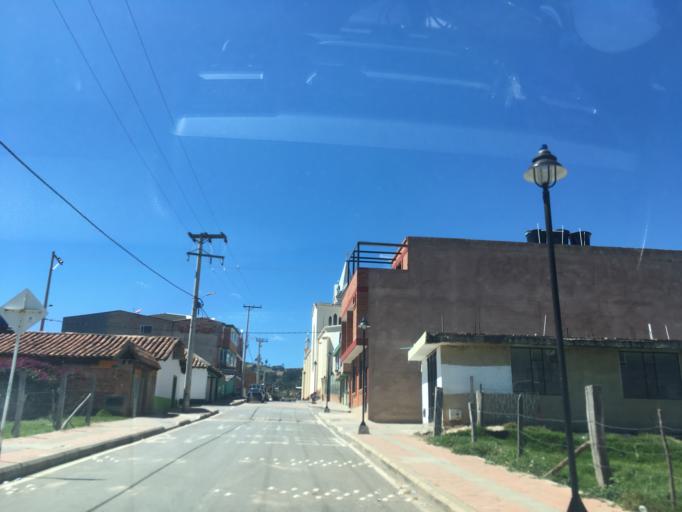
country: CO
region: Boyaca
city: Combita
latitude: 5.6336
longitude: -73.3226
